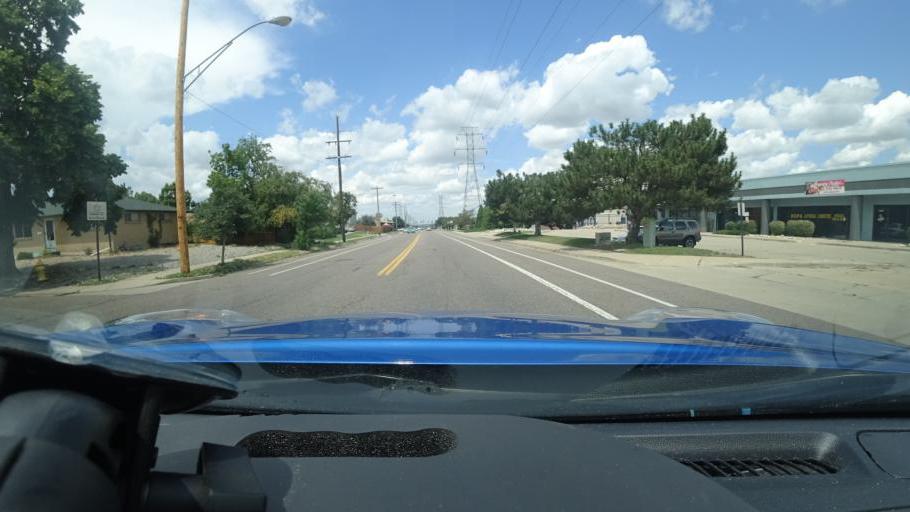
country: US
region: Colorado
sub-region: Adams County
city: Aurora
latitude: 39.7083
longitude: -104.8283
